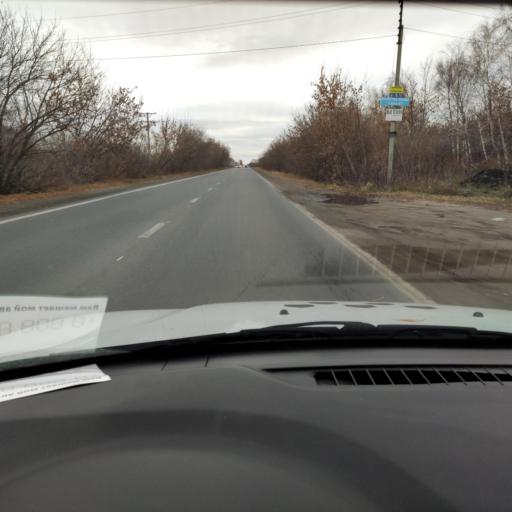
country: RU
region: Samara
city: Tol'yatti
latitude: 53.5589
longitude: 49.3605
